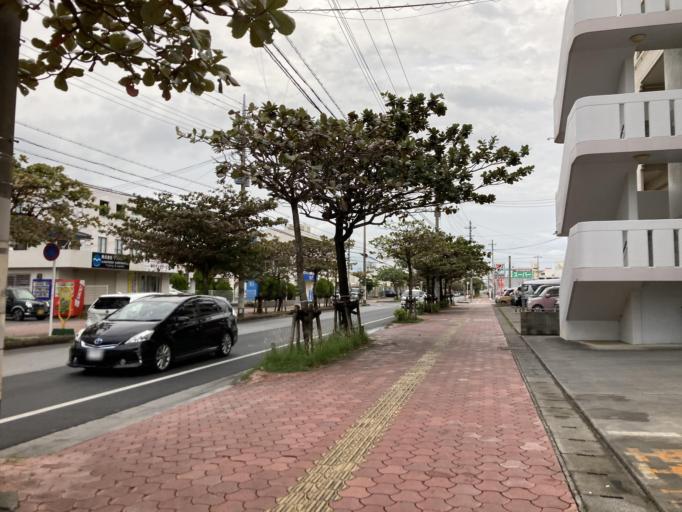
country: JP
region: Okinawa
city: Okinawa
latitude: 26.3191
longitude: 127.8260
